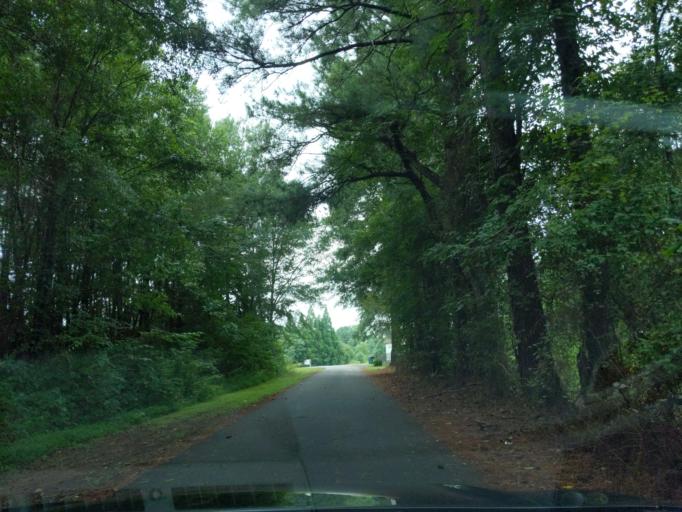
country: US
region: South Carolina
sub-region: Cherokee County
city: East Gaffney
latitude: 35.1220
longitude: -81.5923
